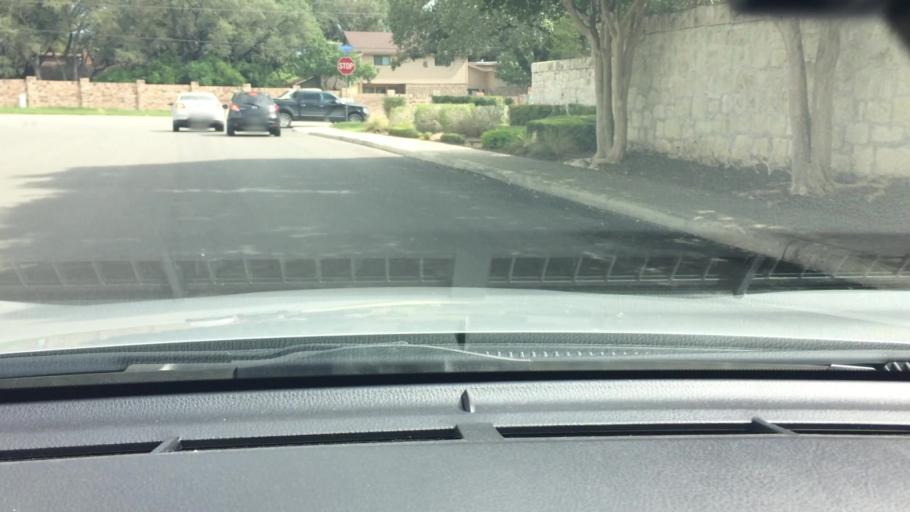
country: US
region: Texas
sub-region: Bexar County
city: Shavano Park
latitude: 29.5634
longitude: -98.5621
